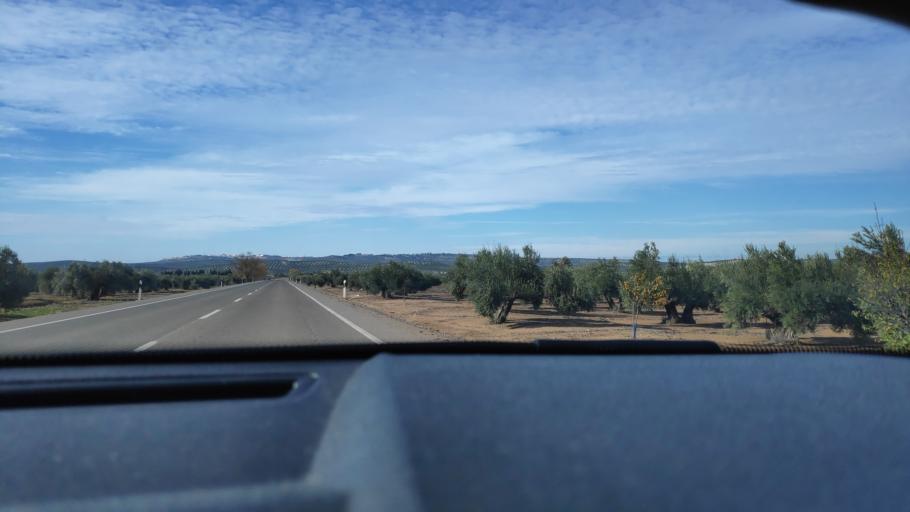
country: ES
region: Andalusia
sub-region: Provincia de Jaen
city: Higuera de Calatrava
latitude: 37.8436
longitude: -4.1153
